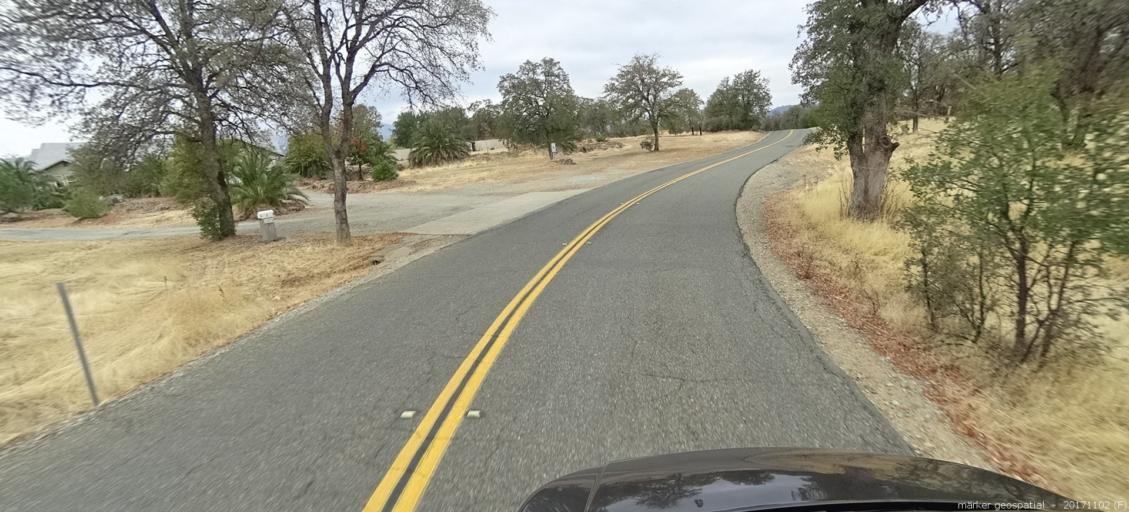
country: US
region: California
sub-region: Shasta County
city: Redding
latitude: 40.6233
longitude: -122.4309
